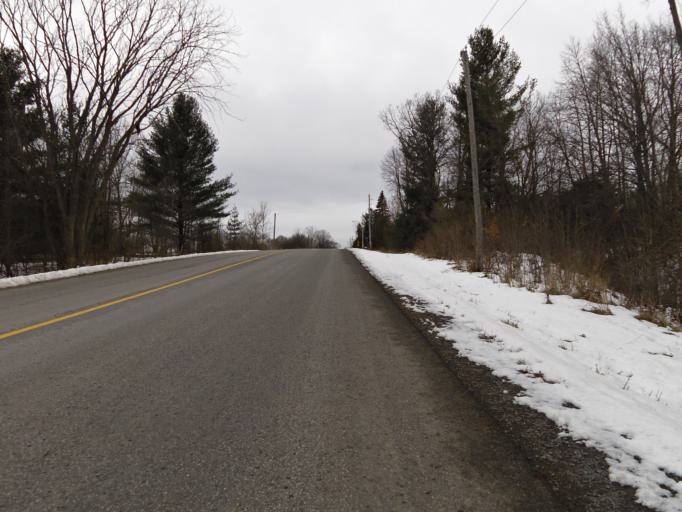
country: CA
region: Ontario
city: Carleton Place
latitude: 45.3593
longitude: -76.1180
